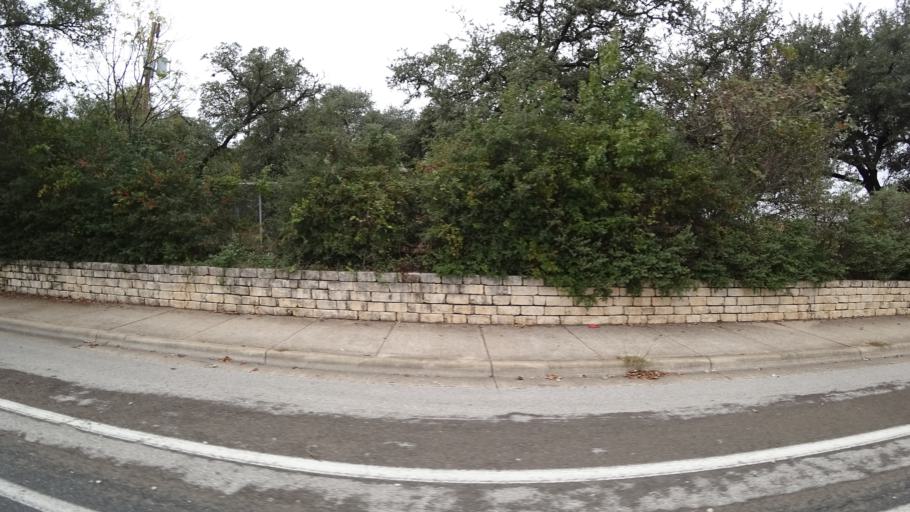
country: US
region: Texas
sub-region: Travis County
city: Shady Hollow
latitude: 30.2104
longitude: -97.8768
